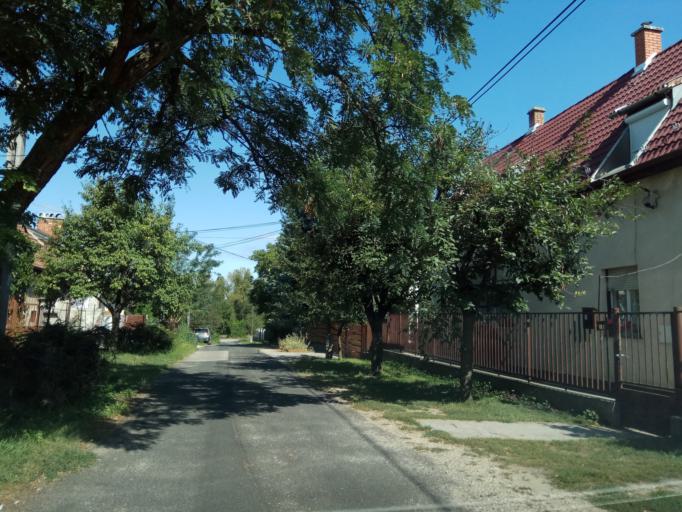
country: HU
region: Pest
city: Pecel
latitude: 47.4925
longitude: 19.3036
